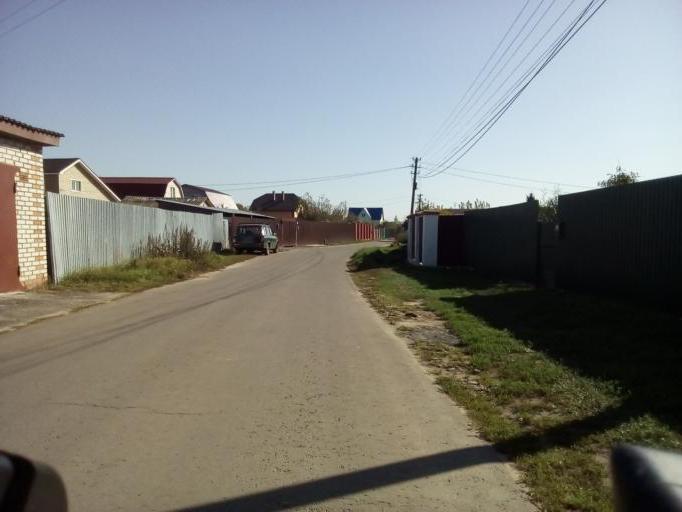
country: RU
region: Moskovskaya
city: Ramenskoye
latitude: 55.5500
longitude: 38.2838
